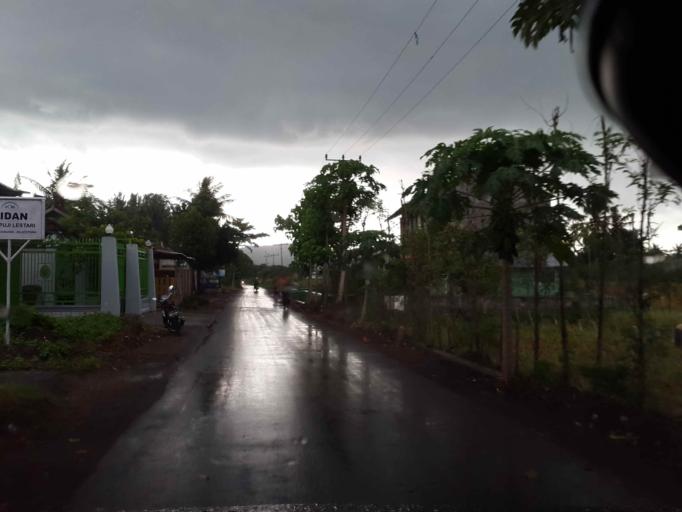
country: ID
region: West Nusa Tenggara
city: Karangkebon Timur
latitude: -8.6591
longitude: 116.1266
